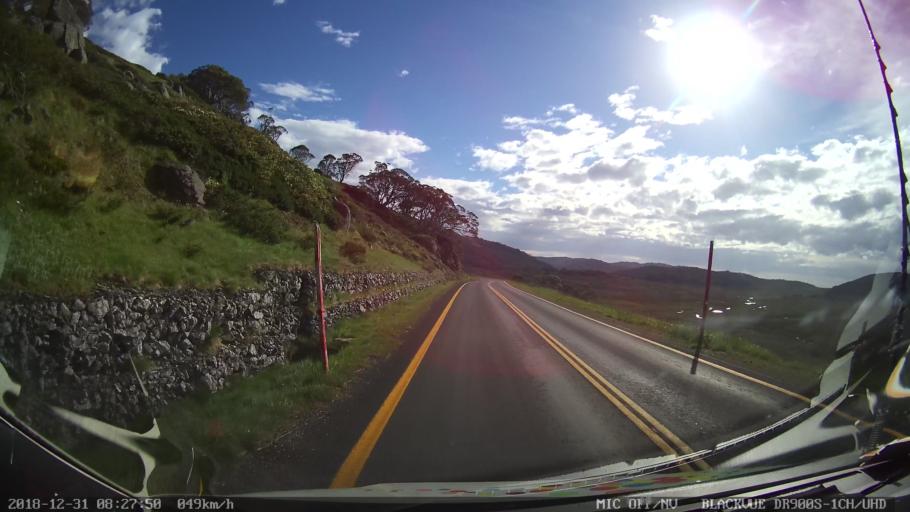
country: AU
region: New South Wales
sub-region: Snowy River
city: Jindabyne
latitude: -36.4305
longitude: 148.3412
